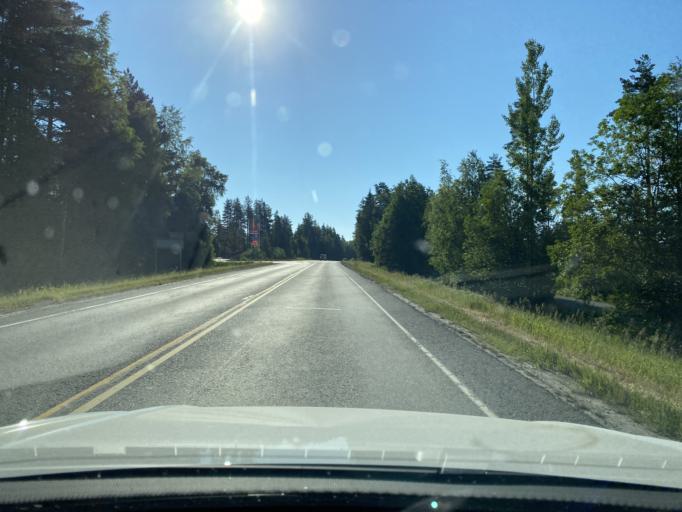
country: FI
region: Haeme
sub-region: Forssa
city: Tammela
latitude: 60.8300
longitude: 23.7218
